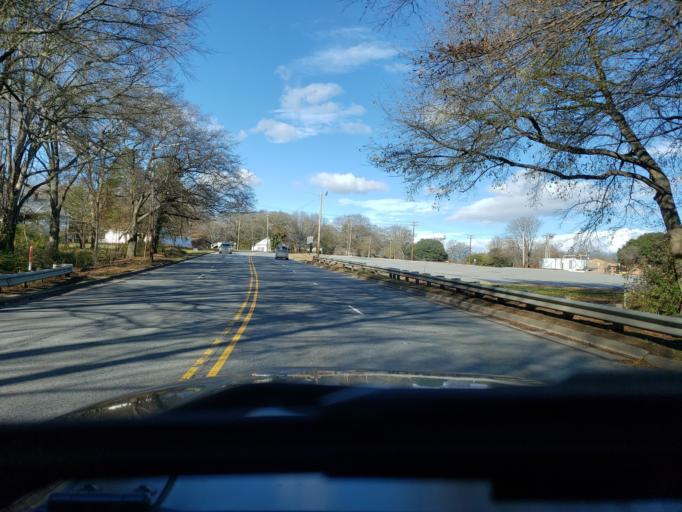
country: US
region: North Carolina
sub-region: Cleveland County
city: Shelby
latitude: 35.2729
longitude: -81.5399
